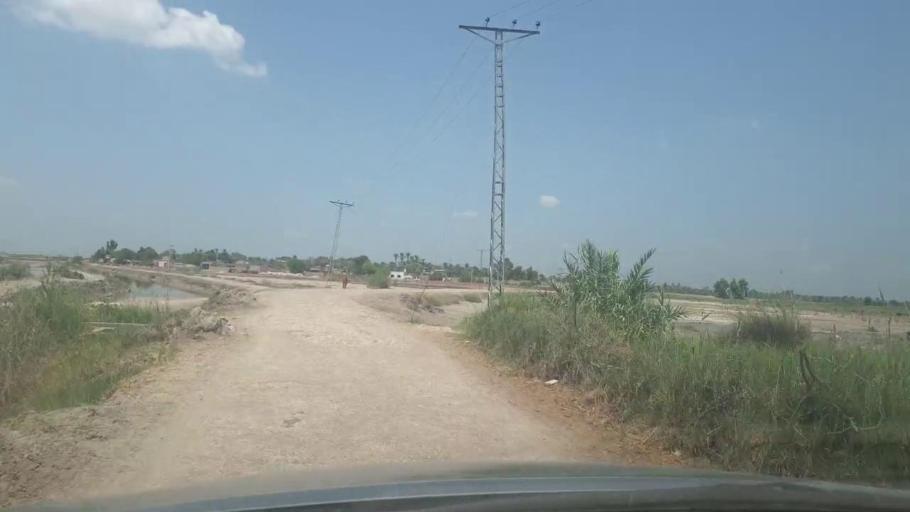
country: PK
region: Sindh
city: Kot Diji
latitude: 27.4174
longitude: 68.7361
